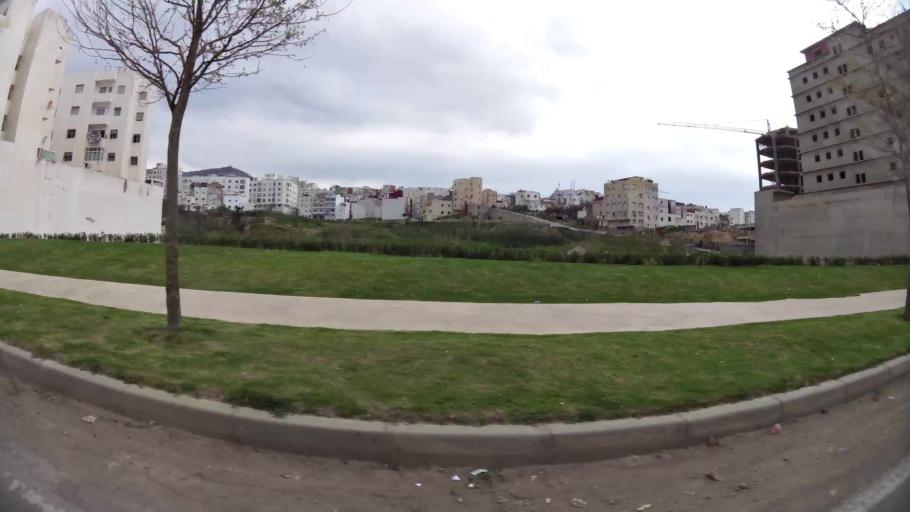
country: MA
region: Tanger-Tetouan
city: Tetouan
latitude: 35.5626
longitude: -5.3745
